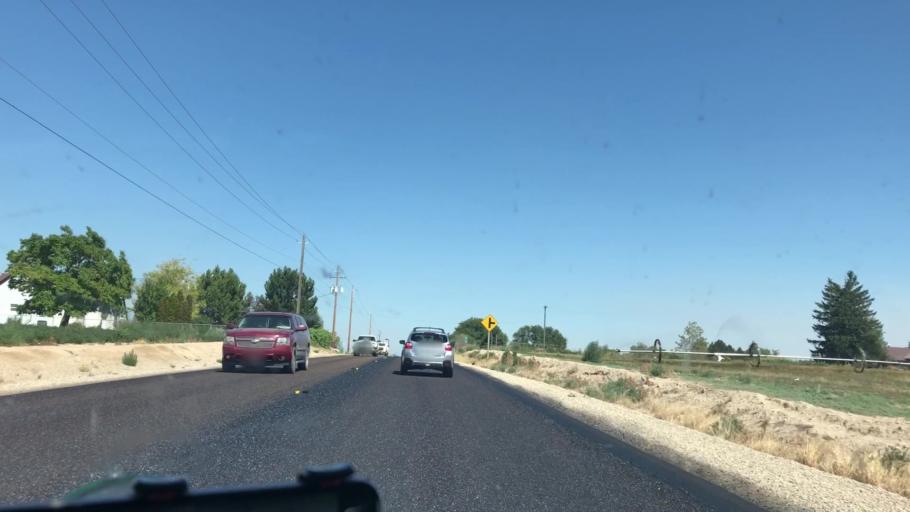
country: US
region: Idaho
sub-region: Canyon County
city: Caldwell
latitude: 43.6037
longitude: -116.7265
